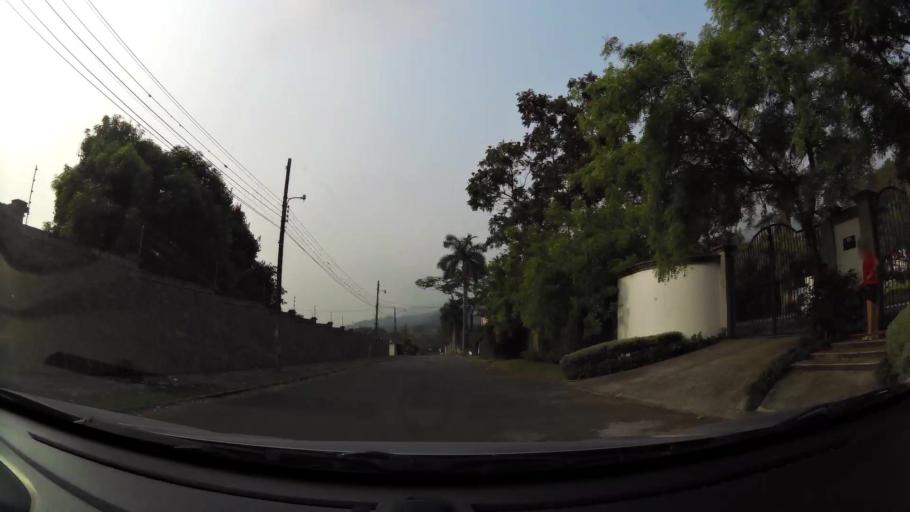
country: HN
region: Cortes
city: Armenta
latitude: 15.4953
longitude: -88.0483
